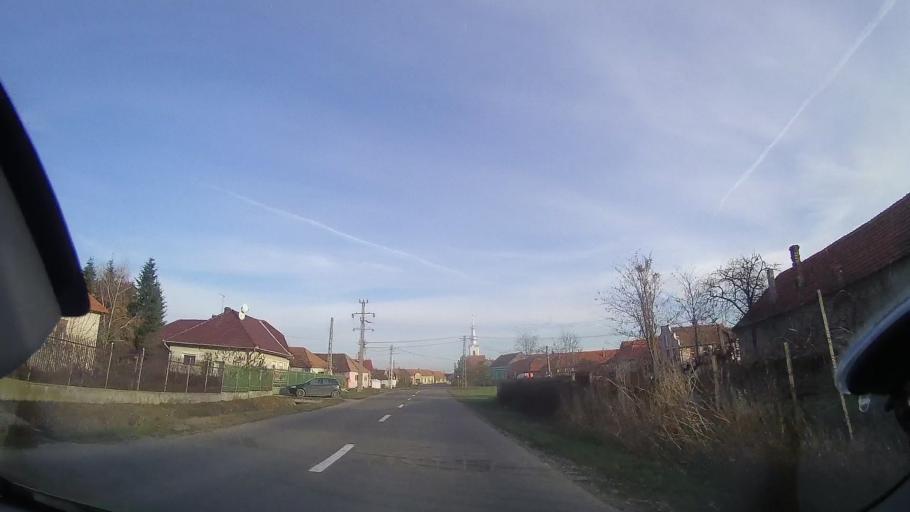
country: RO
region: Bihor
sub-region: Comuna Tetchea
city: Hotar
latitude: 47.0552
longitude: 22.2720
